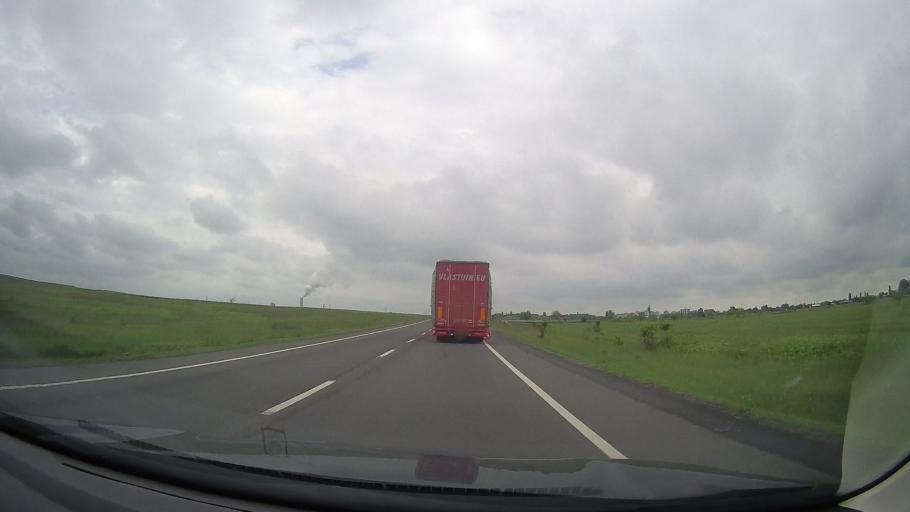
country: RO
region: Dolj
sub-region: Municipiul Craiova
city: Cernele
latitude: 44.3571
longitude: 23.7683
